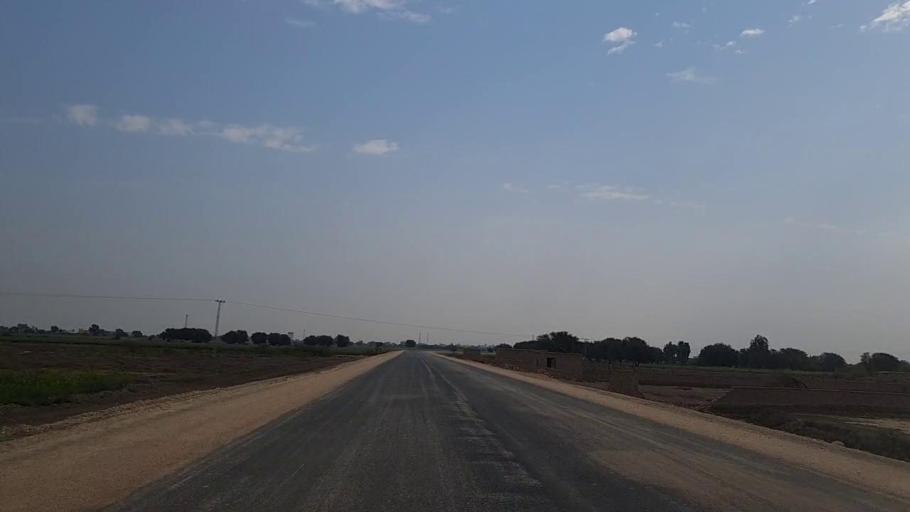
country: PK
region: Sindh
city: Naukot
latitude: 24.9818
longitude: 69.2846
